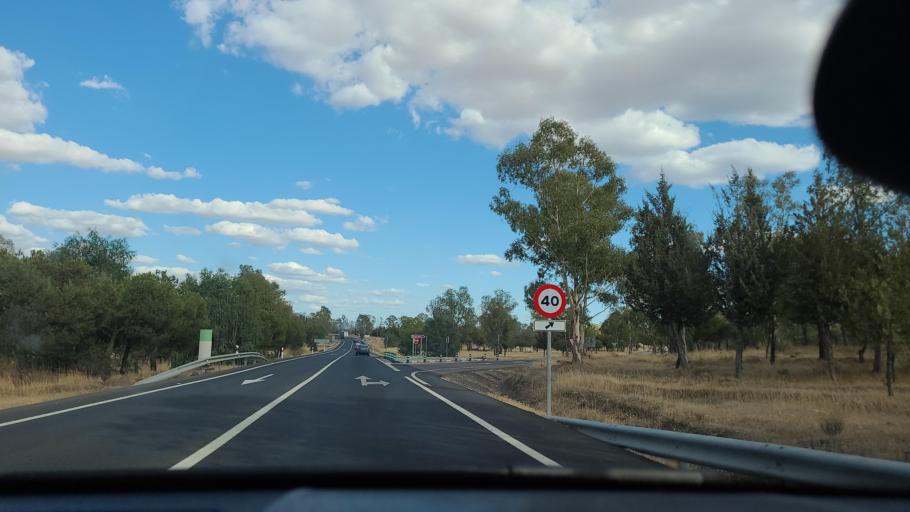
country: ES
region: Extremadura
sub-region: Provincia de Badajoz
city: Berlanga
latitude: 38.2737
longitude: -5.8165
